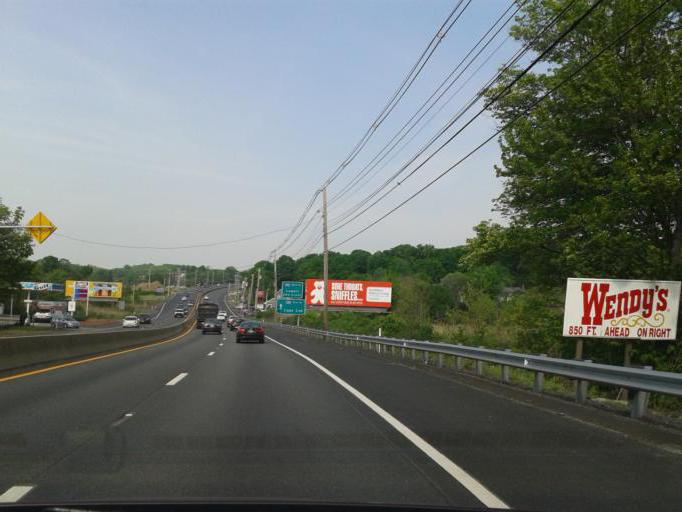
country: US
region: Massachusetts
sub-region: Worcester County
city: Southborough
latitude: 42.2904
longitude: -71.5540
